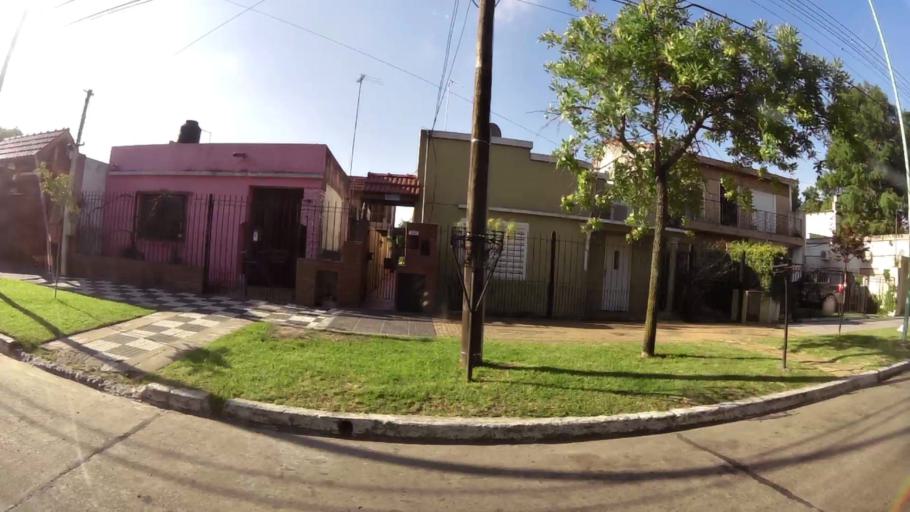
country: AR
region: Buenos Aires
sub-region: Partido de Merlo
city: Merlo
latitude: -34.6715
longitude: -58.7301
